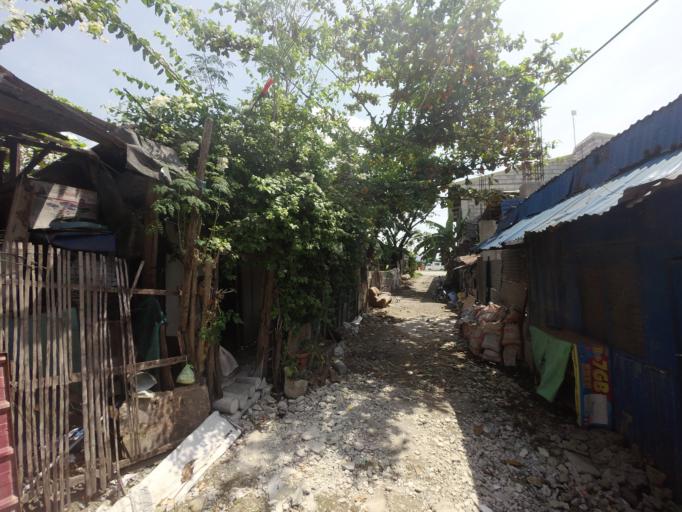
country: PH
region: Calabarzon
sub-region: Province of Rizal
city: Taguig
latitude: 14.5324
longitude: 121.1102
